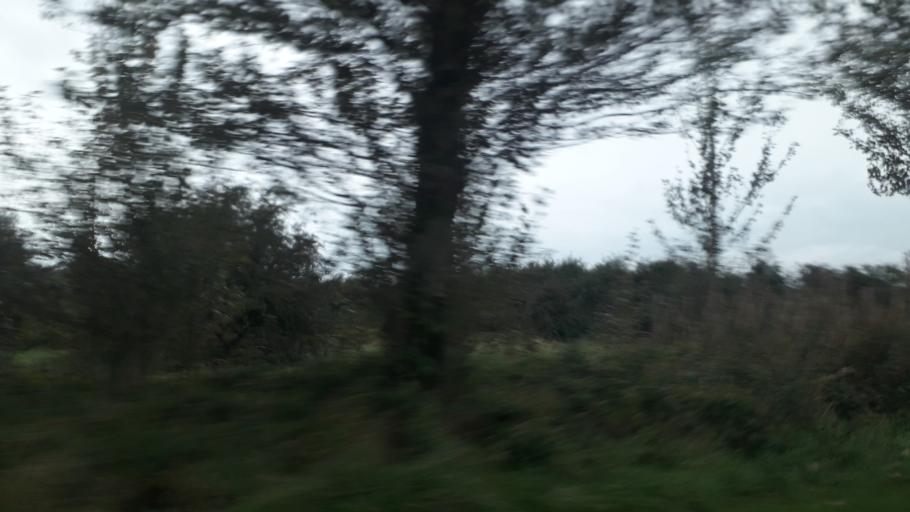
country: IE
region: Leinster
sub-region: An Longfort
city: Lanesborough
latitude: 53.7462
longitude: -7.9376
